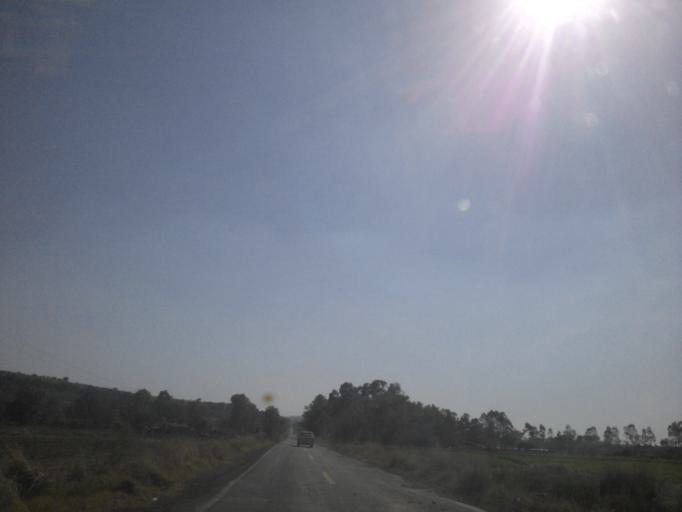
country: MX
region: Jalisco
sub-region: Arandas
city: Santiaguito (Santiaguito de Velazquez)
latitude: 20.7991
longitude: -102.2412
